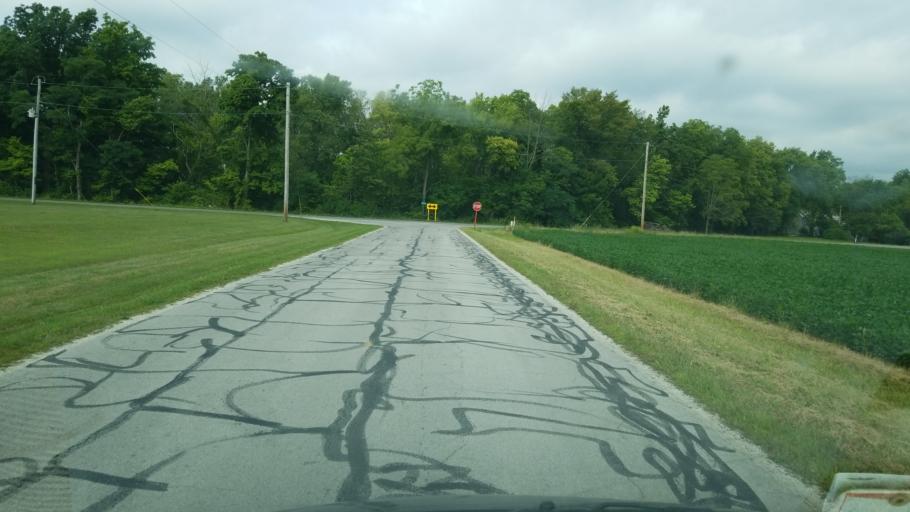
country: US
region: Ohio
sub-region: Seneca County
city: Tiffin
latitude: 41.1896
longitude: -83.1404
